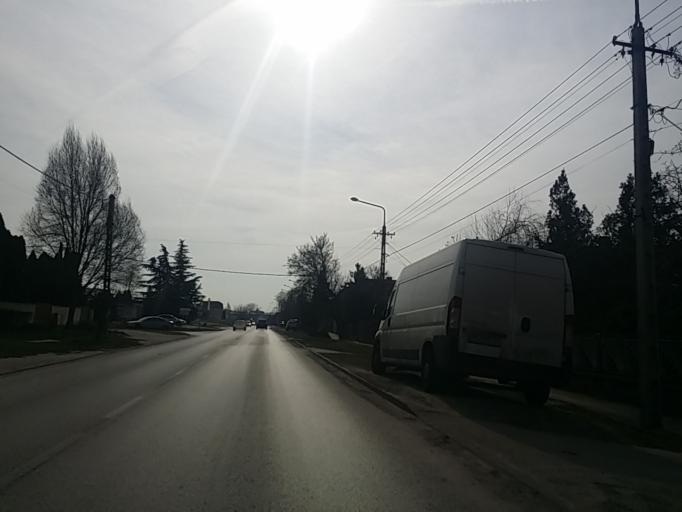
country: HU
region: Pest
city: Fot
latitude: 47.6231
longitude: 19.1871
